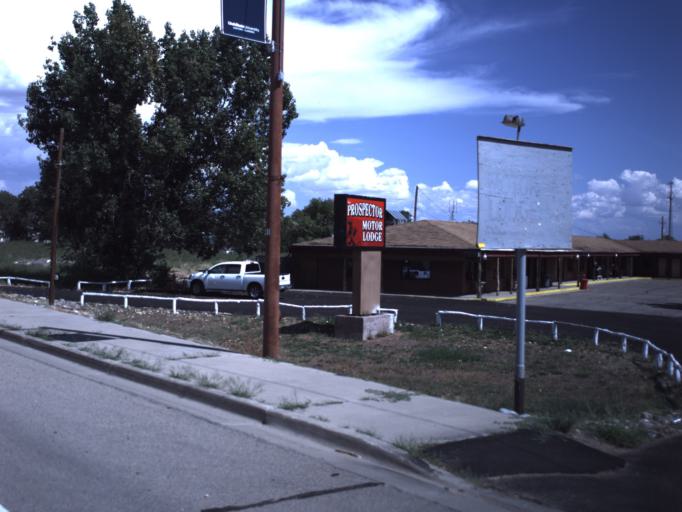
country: US
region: Utah
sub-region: San Juan County
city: Blanding
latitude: 37.6169
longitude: -109.4783
